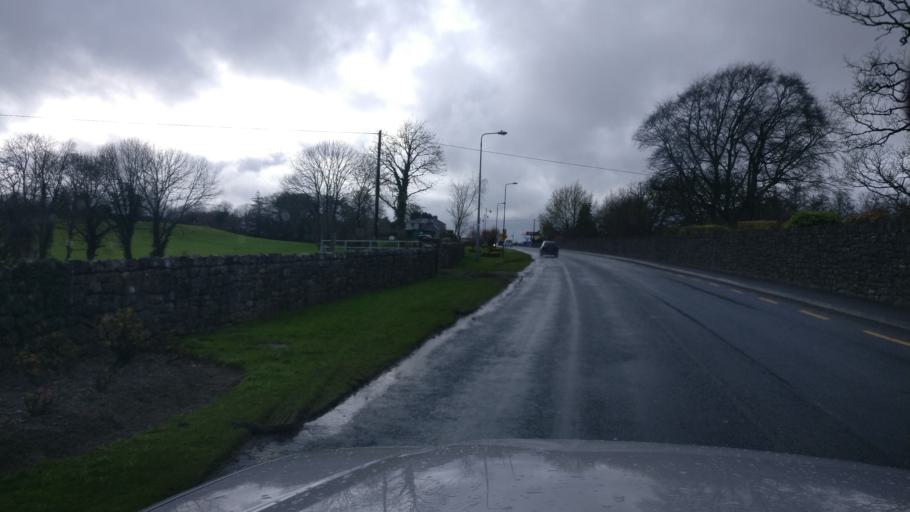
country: IE
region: Leinster
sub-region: An Iarmhi
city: Athlone
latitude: 53.4270
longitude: -8.0161
